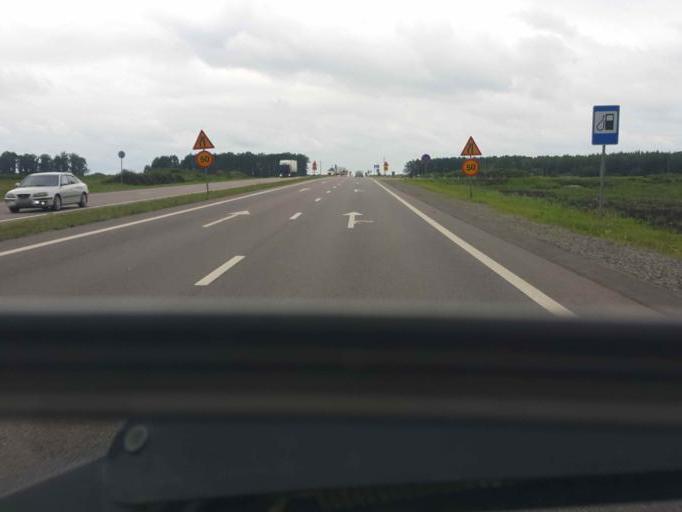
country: RU
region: Tambov
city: Zavoronezhskoye
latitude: 52.8894
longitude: 40.7032
